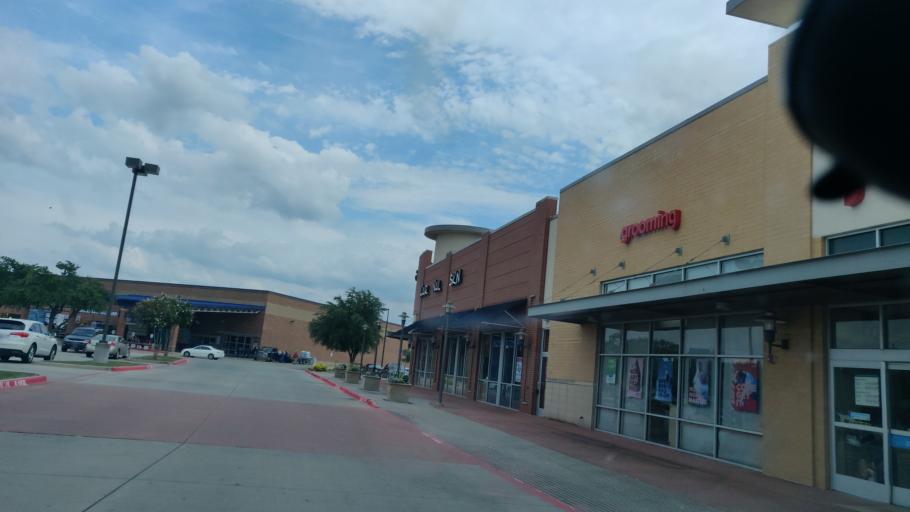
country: US
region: Texas
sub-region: Dallas County
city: Sachse
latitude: 32.9451
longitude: -96.6122
